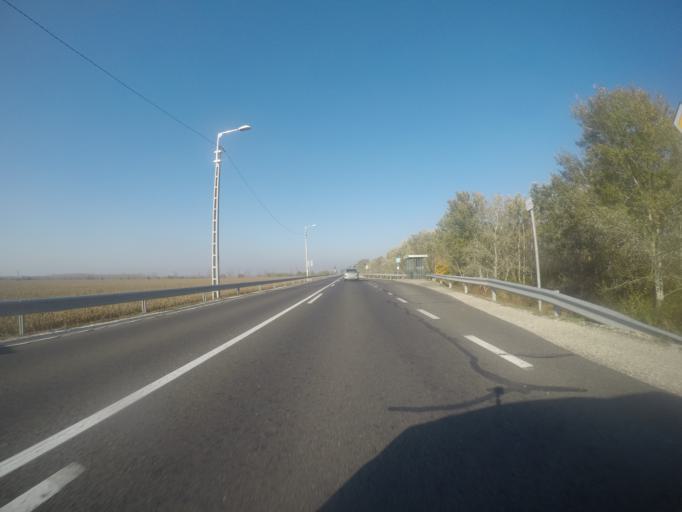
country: HU
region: Fejer
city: Ivancsa
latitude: 47.1808
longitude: 18.8687
